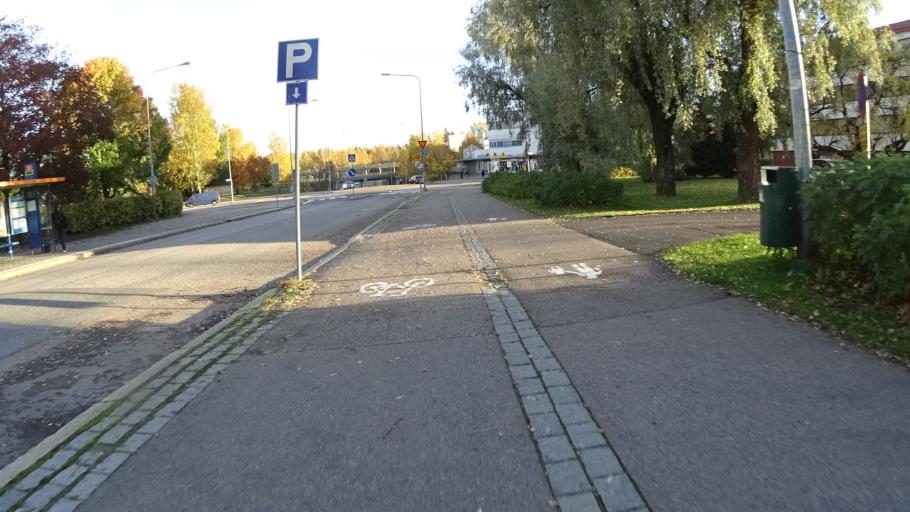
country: FI
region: Uusimaa
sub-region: Helsinki
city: Helsinki
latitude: 60.2296
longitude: 24.9626
